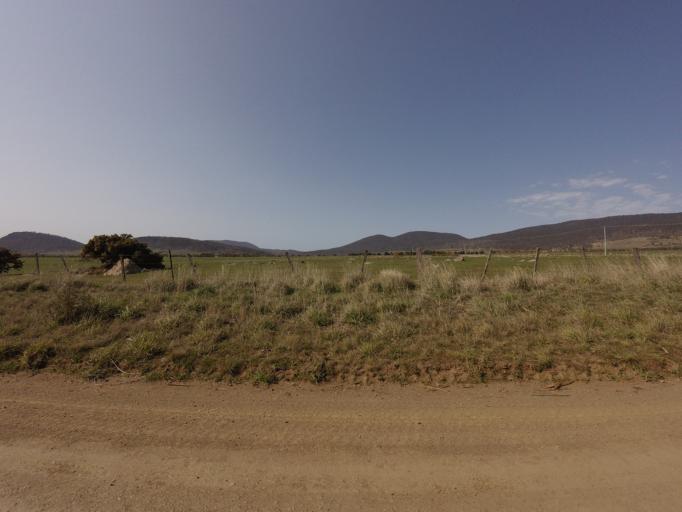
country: AU
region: Tasmania
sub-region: Break O'Day
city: St Helens
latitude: -41.8239
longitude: 147.9348
